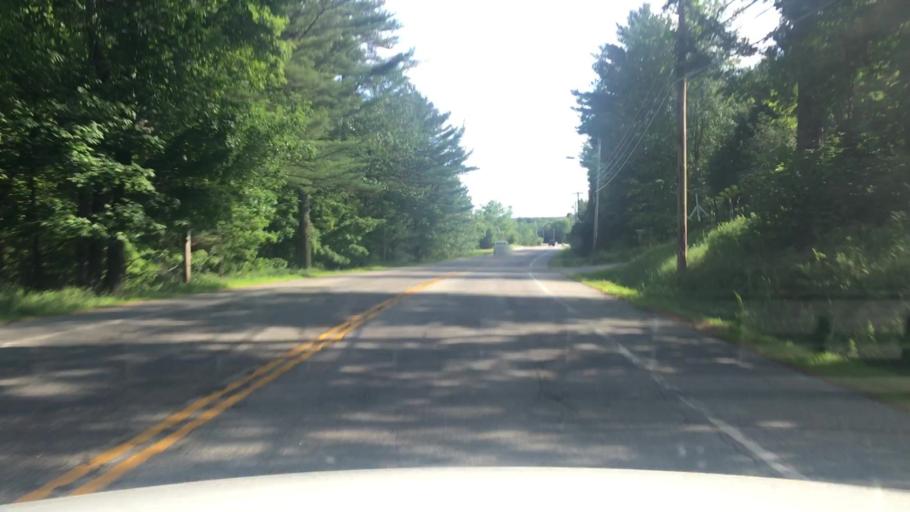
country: US
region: Maine
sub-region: Franklin County
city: Wilton
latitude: 44.5627
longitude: -70.2329
